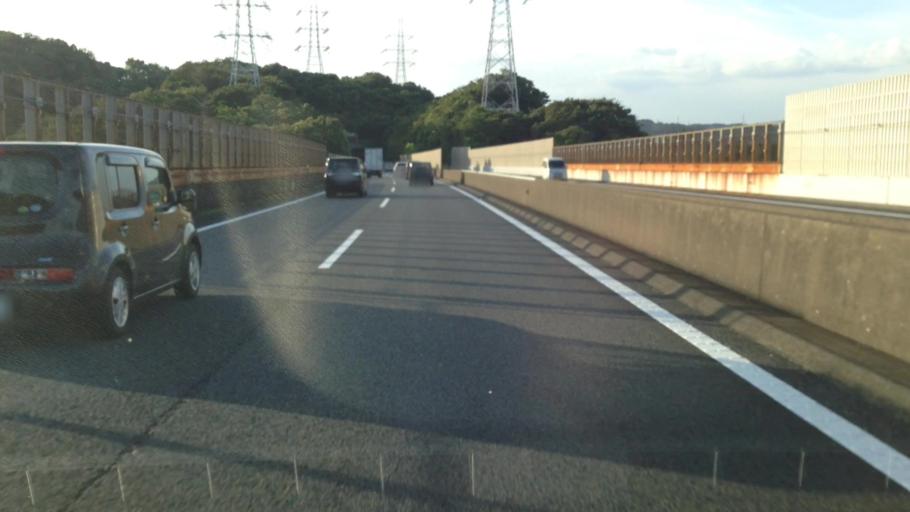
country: JP
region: Kanagawa
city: Zushi
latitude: 35.3199
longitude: 139.6048
